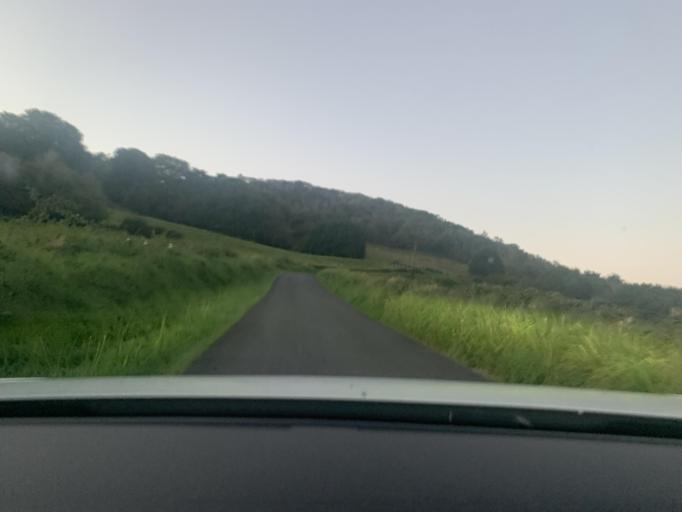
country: IE
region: Connaught
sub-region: County Leitrim
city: Manorhamilton
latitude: 54.2615
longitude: -8.2954
